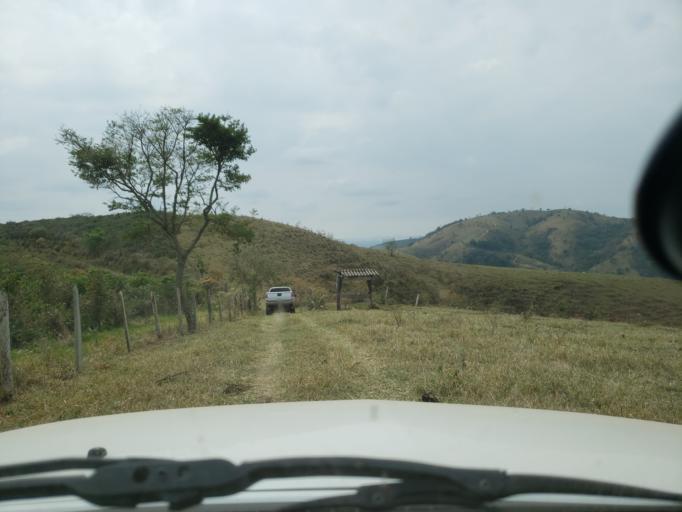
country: BR
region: Minas Gerais
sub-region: Jacutinga
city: Jacutinga
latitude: -22.3426
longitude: -46.5865
